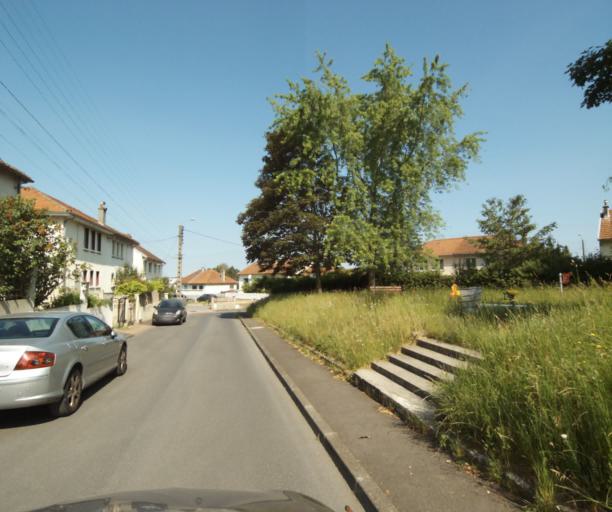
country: FR
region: Champagne-Ardenne
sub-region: Departement des Ardennes
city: Charleville-Mezieres
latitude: 49.7785
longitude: 4.7043
